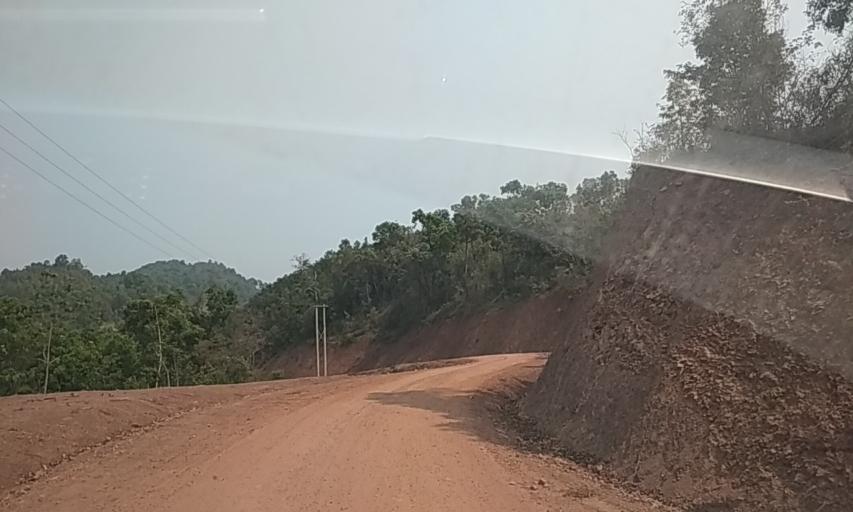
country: VN
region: Huyen Dien Bien
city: Dien Bien Phu
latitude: 21.4677
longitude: 102.7715
